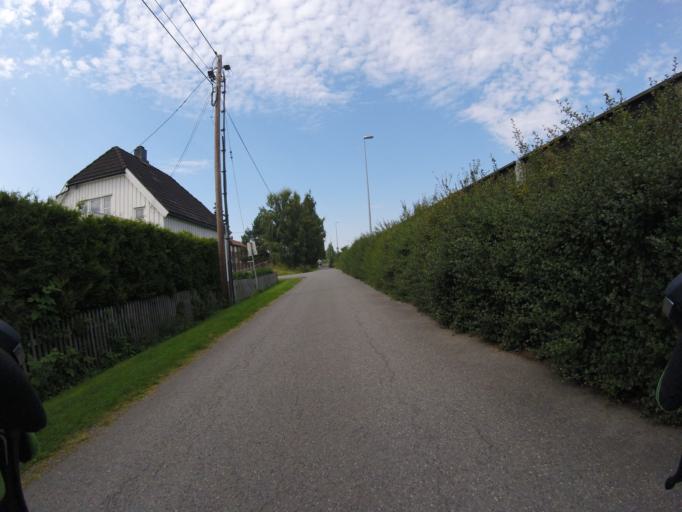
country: NO
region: Akershus
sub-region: Skedsmo
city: Lillestrom
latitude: 59.9549
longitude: 11.0745
